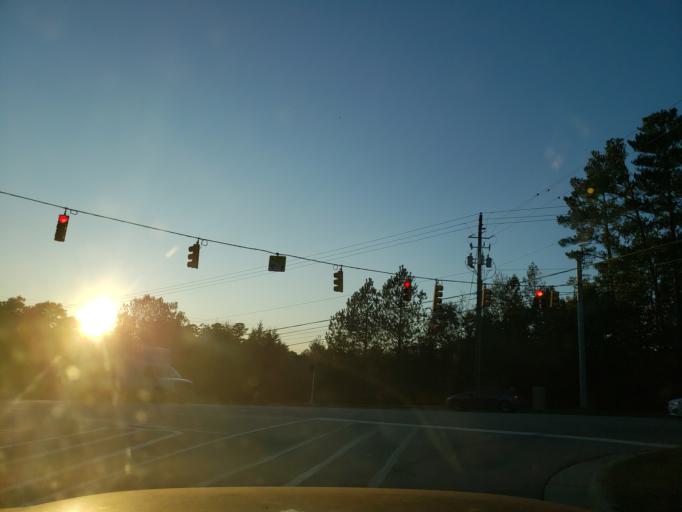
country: US
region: North Carolina
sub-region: Wake County
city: Apex
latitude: 35.7419
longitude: -78.8231
